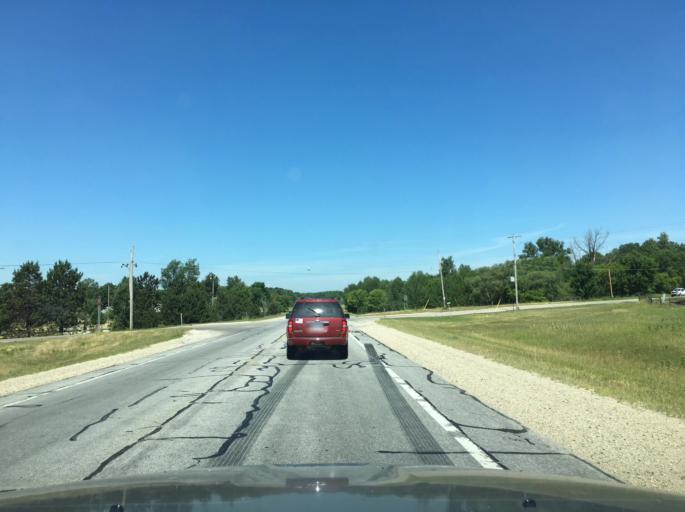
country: US
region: Michigan
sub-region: Osceola County
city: Reed City
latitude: 43.8795
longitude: -85.5024
